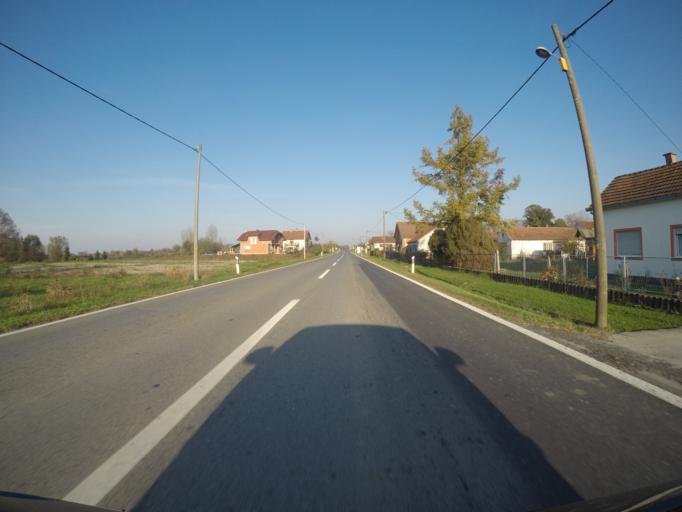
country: HR
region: Virovitick-Podravska
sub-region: Grad Virovitica
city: Virovitica
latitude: 45.8884
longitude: 17.4173
